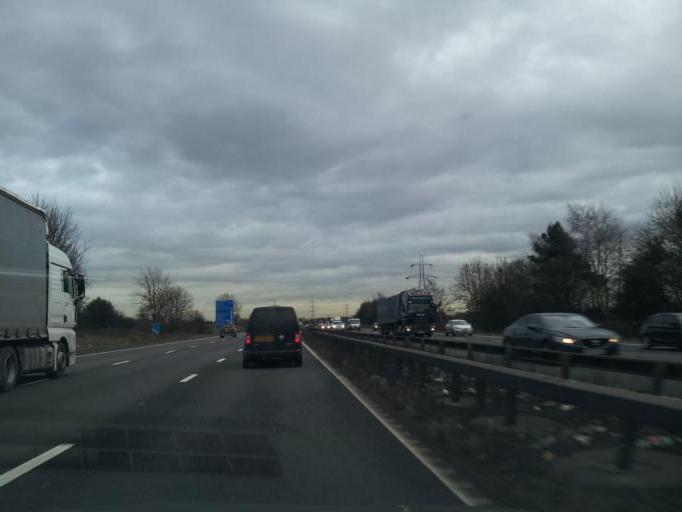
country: GB
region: England
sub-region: Warwickshire
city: Exhall
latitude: 52.4663
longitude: -1.5062
